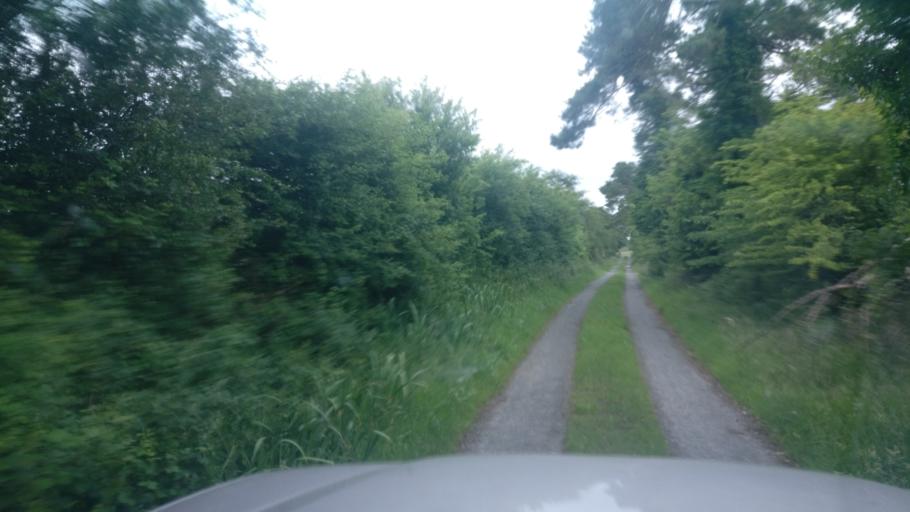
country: IE
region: Connaught
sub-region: County Galway
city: Ballinasloe
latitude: 53.2956
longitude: -8.3629
